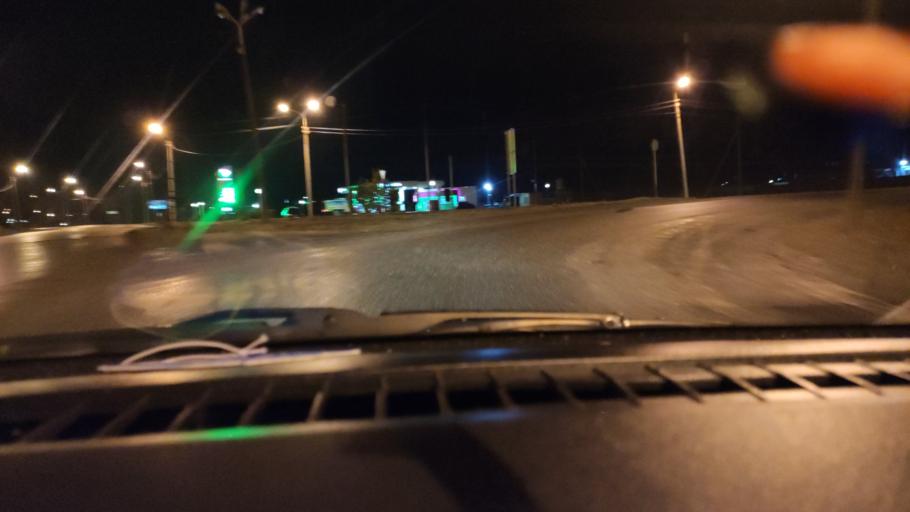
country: RU
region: Udmurtiya
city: Pirogovo
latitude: 56.7344
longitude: 53.2767
